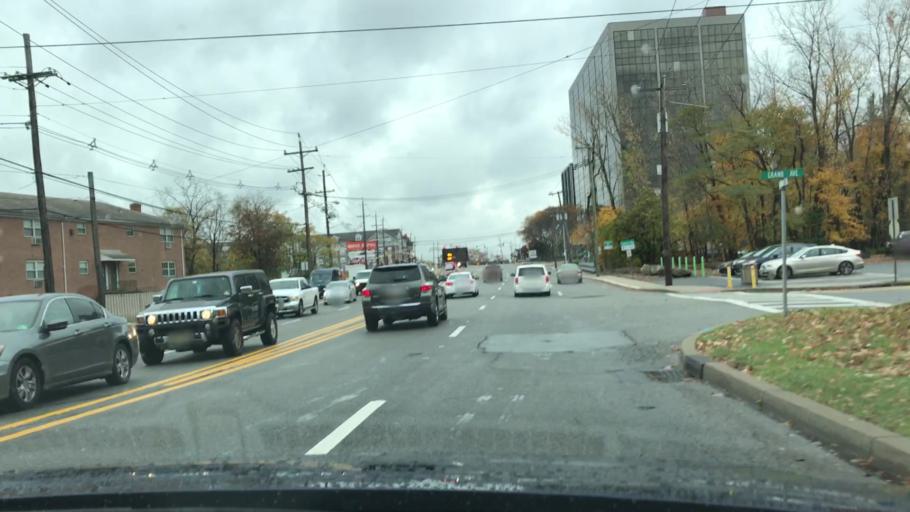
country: US
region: New Jersey
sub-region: Bergen County
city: River Edge
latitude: 40.9119
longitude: -74.0335
